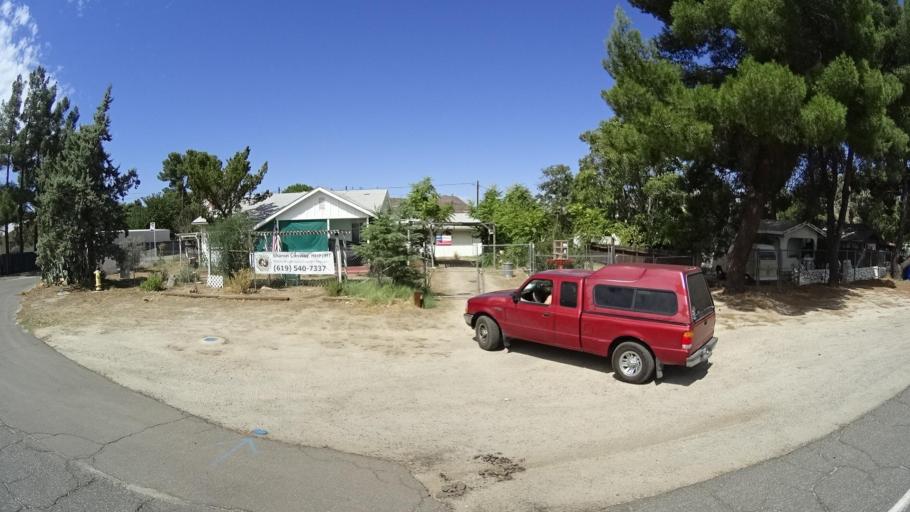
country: MX
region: Baja California
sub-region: Tecate
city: Cereso del Hongo
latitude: 32.6177
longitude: -116.1842
